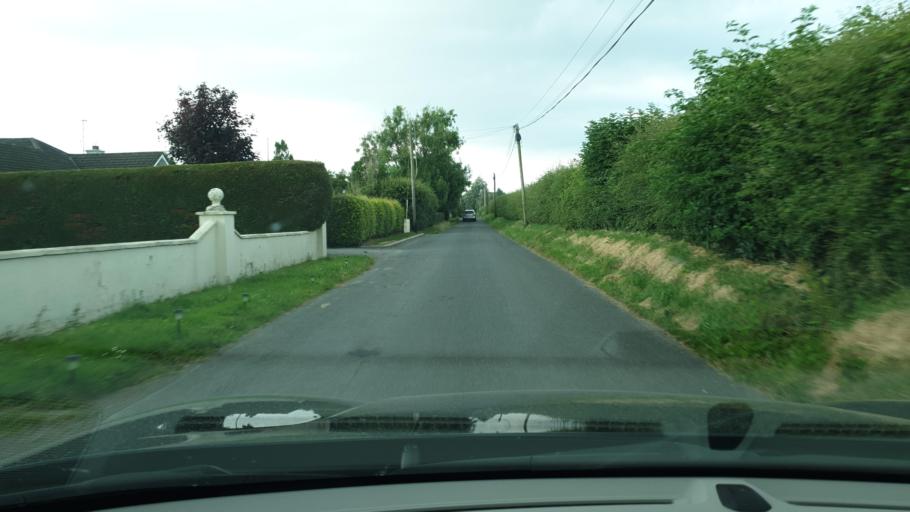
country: IE
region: Leinster
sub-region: An Mhi
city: Dunshaughlin
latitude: 53.4996
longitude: -6.5129
